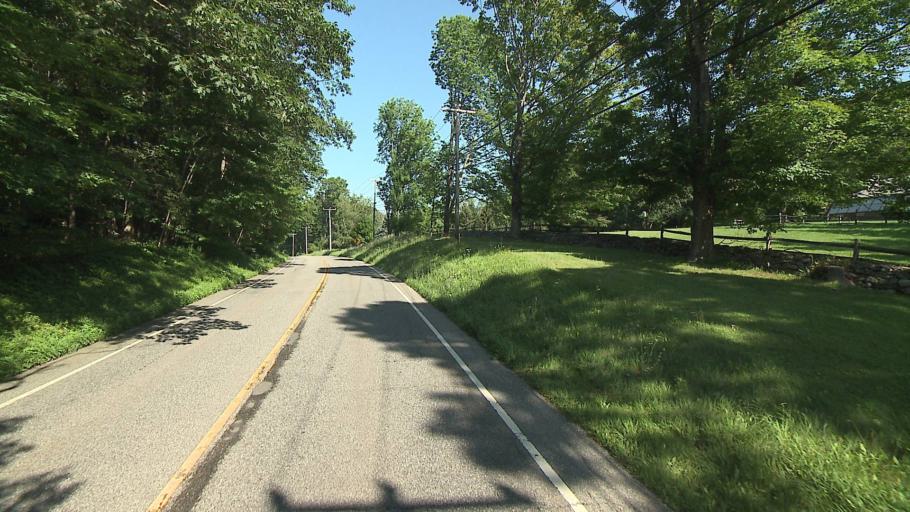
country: US
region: Connecticut
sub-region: Litchfield County
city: Kent
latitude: 41.8411
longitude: -73.4335
